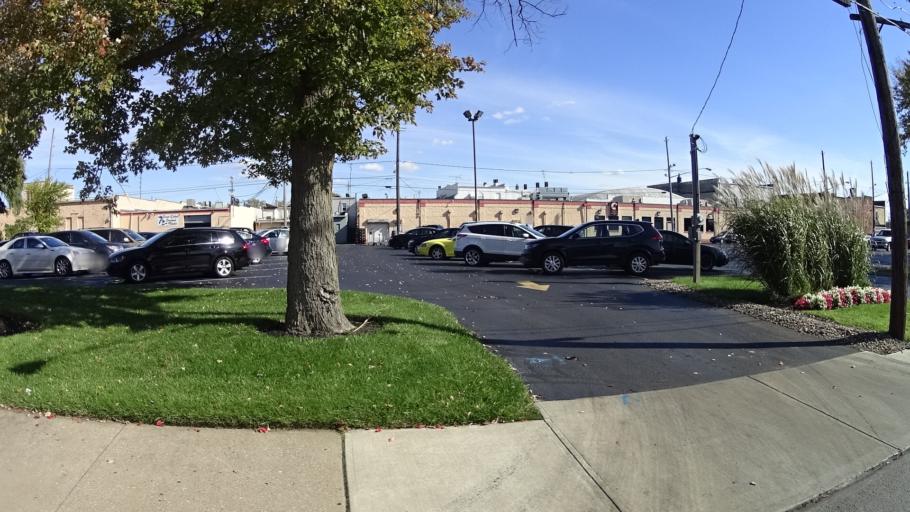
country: US
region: Ohio
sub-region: Lorain County
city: Lorain
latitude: 41.4533
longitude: -82.1678
